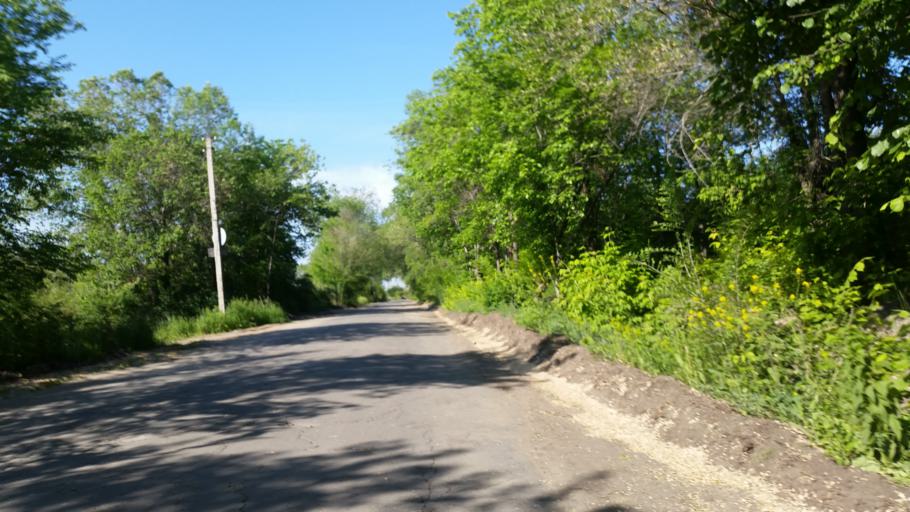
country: RU
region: Ulyanovsk
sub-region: Ulyanovskiy Rayon
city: Ulyanovsk
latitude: 54.3079
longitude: 48.4092
